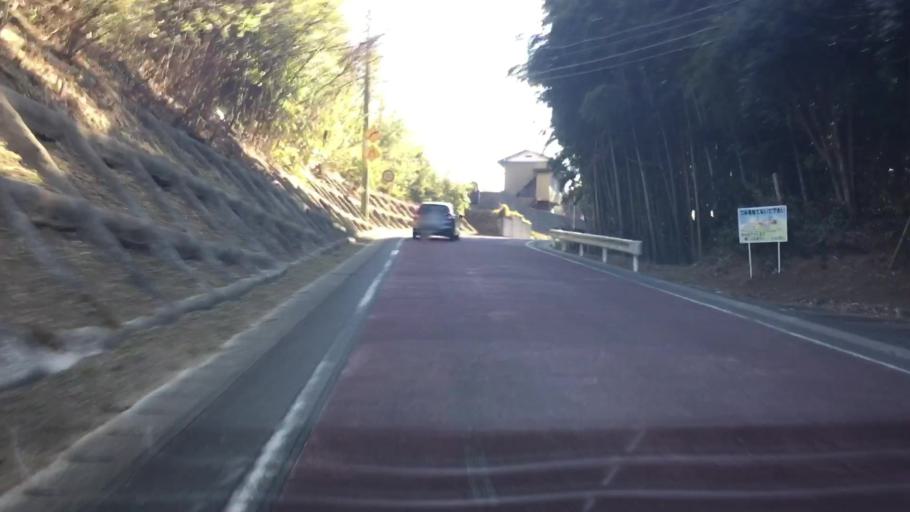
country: JP
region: Chiba
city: Shiroi
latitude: 35.8203
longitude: 140.1193
